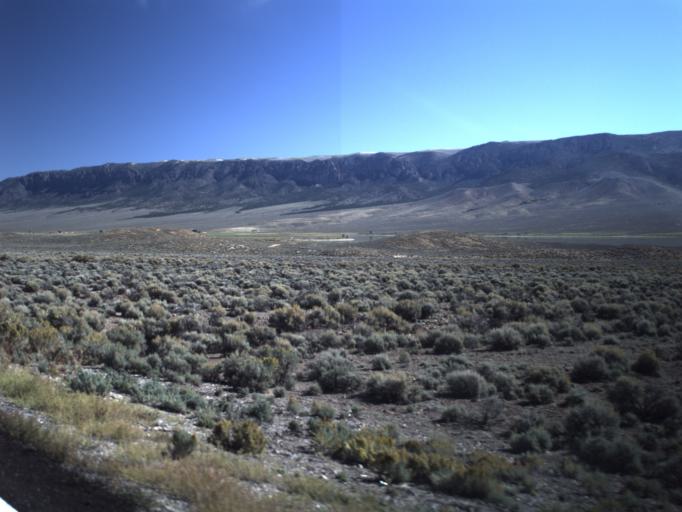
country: US
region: Utah
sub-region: Piute County
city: Junction
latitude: 38.2100
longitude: -112.0041
